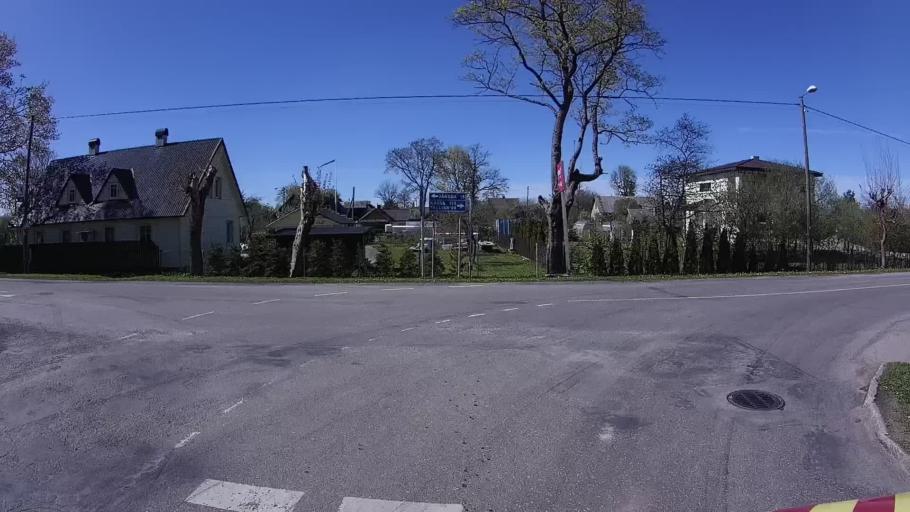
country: EE
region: Laeaene-Virumaa
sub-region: Tapa vald
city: Tapa
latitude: 59.2695
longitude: 25.9630
